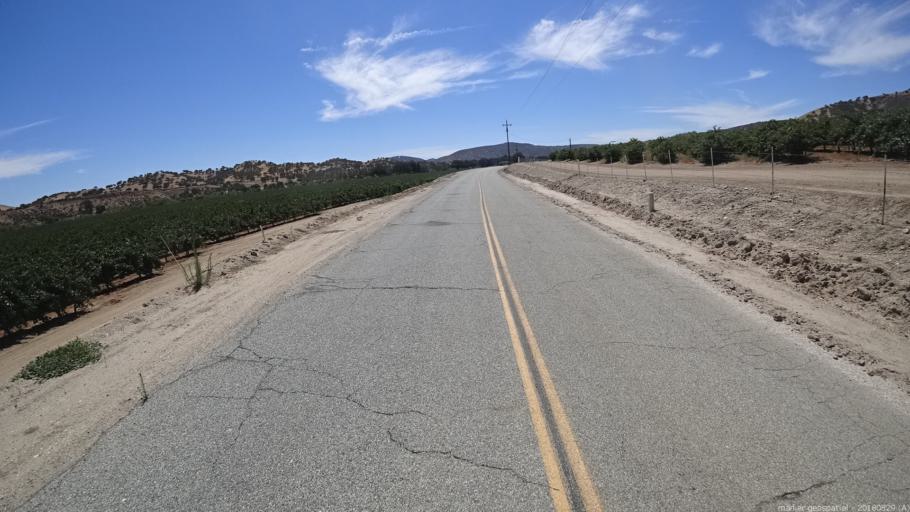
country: US
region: California
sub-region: San Luis Obispo County
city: Lake Nacimiento
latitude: 35.8146
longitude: -120.8460
